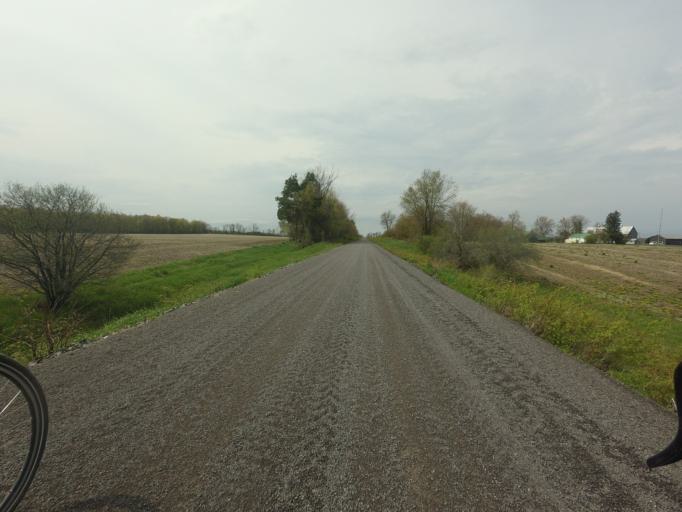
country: CA
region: Ontario
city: Carleton Place
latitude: 45.1789
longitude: -76.1556
